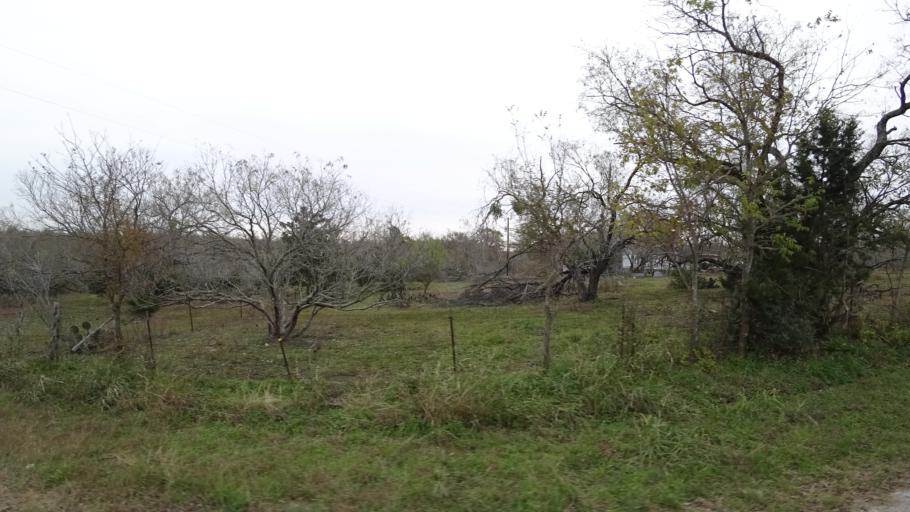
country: US
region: Texas
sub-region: Travis County
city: Garfield
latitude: 30.1190
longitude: -97.5654
